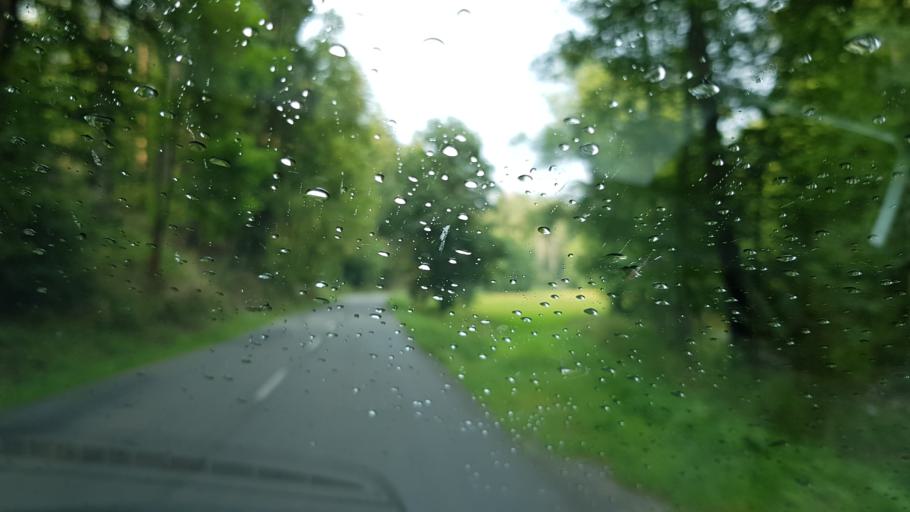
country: CZ
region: Olomoucky
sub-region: Okres Sumperk
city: Hanusovice
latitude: 50.0915
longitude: 16.8490
